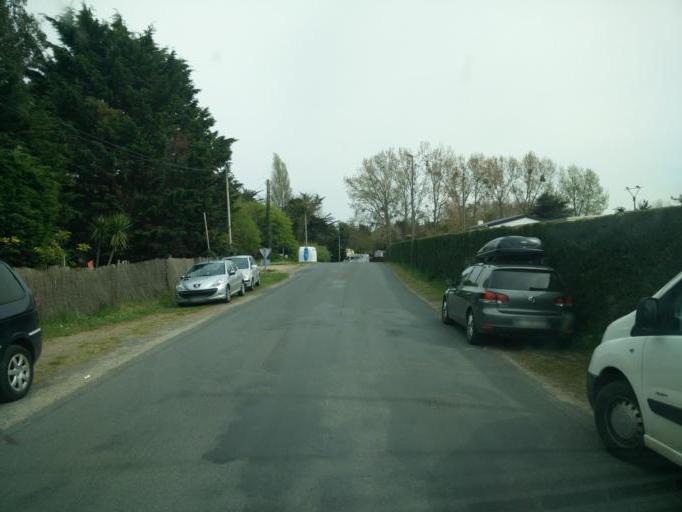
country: FR
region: Brittany
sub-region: Departement des Cotes-d'Armor
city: Plurien
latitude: 48.6515
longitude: -2.3559
